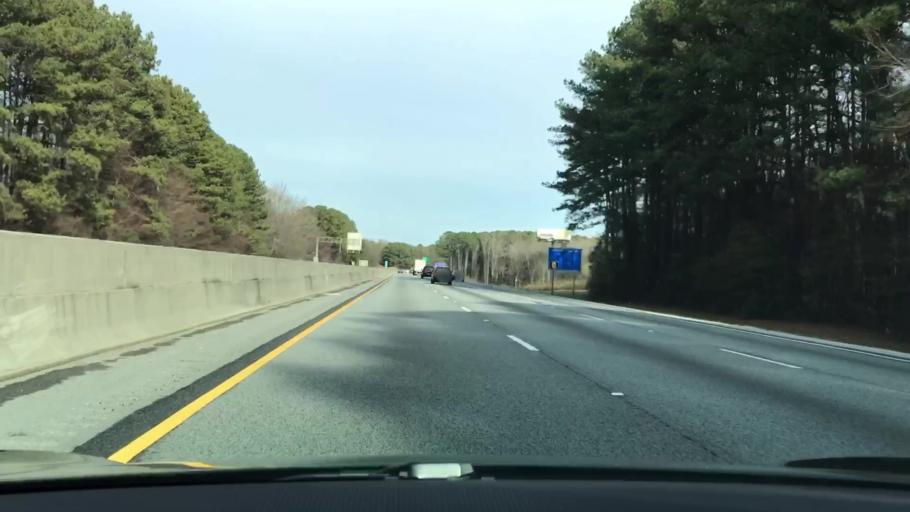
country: US
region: Georgia
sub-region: Newton County
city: Oxford
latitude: 33.6117
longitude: -83.8643
